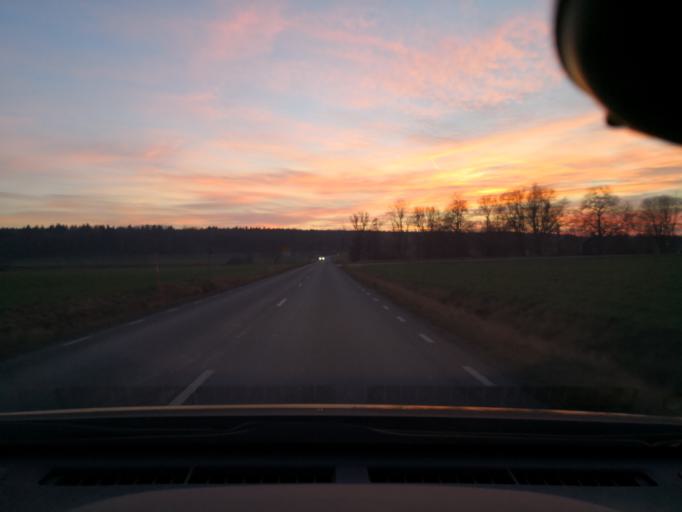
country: SE
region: OErebro
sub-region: Lindesbergs Kommun
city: Fellingsbro
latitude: 59.4272
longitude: 15.5730
